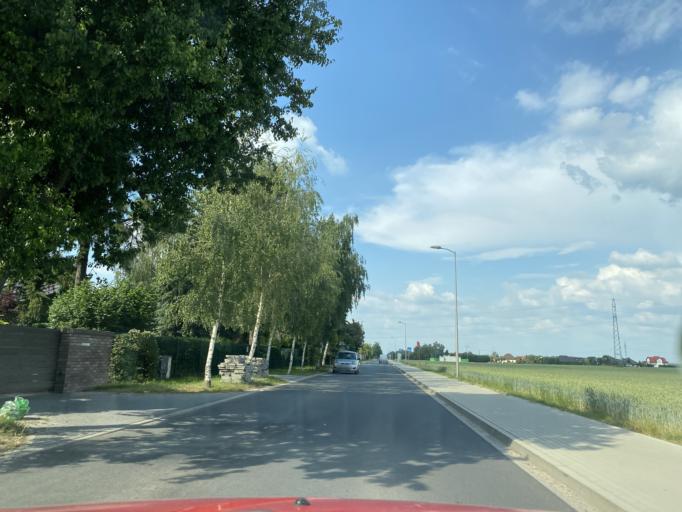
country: PL
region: Greater Poland Voivodeship
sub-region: Powiat poznanski
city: Baranowo
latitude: 52.3915
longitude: 16.7495
